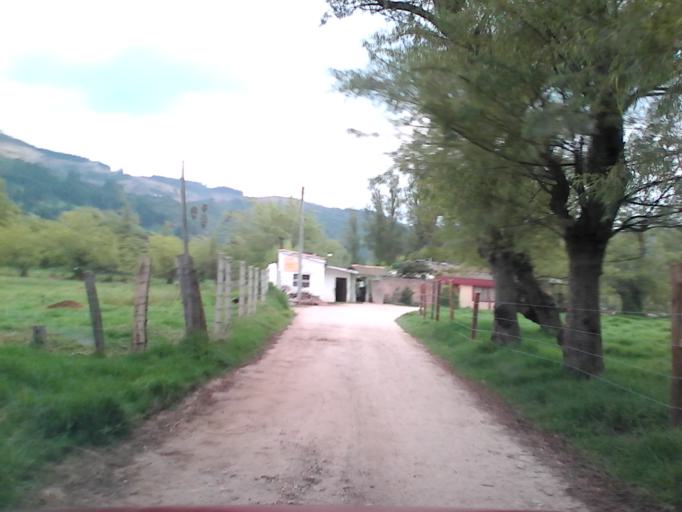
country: CO
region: Boyaca
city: Duitama
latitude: 5.8151
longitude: -73.0130
